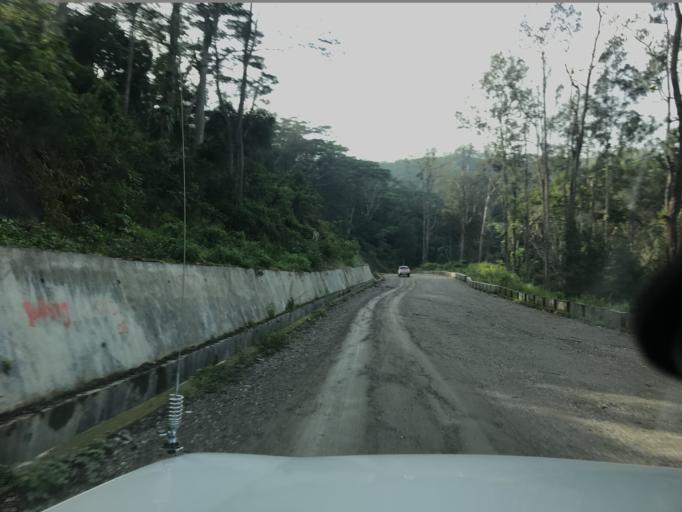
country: TL
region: Aileu
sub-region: Aileu Villa
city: Aileu
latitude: -8.6674
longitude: 125.5534
